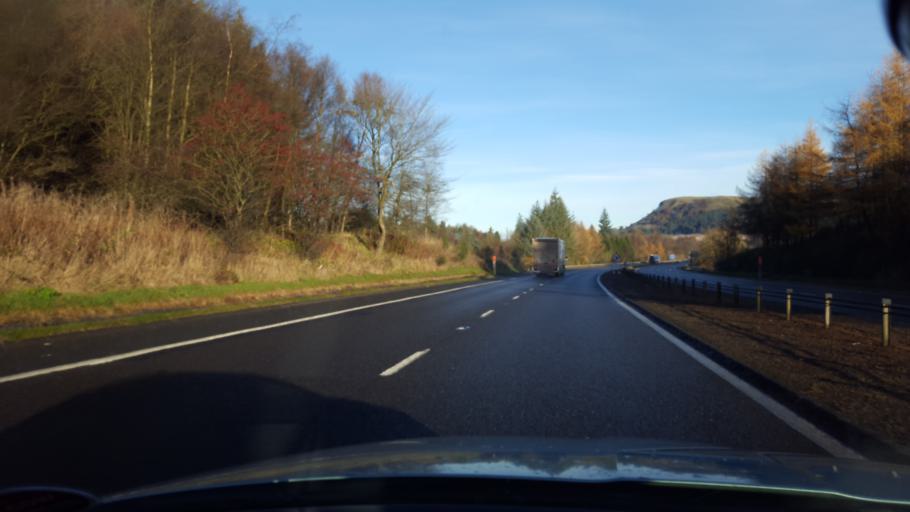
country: GB
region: Scotland
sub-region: Fife
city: Kelty
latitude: 56.1384
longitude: -3.3977
